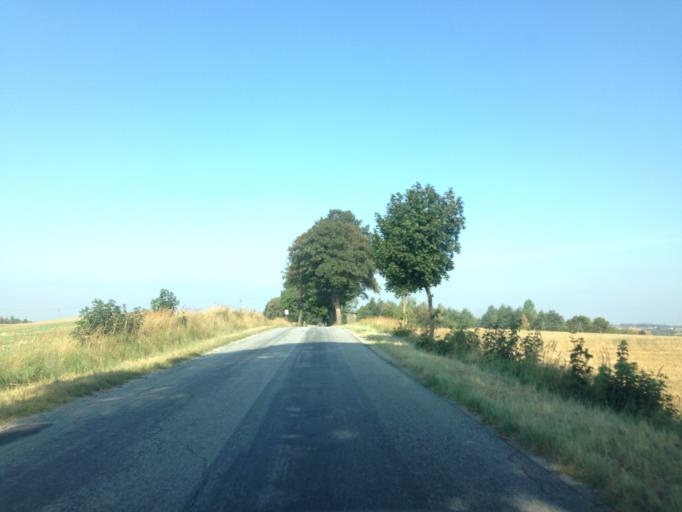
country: PL
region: Kujawsko-Pomorskie
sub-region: Powiat brodnicki
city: Brzozie
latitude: 53.2968
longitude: 19.6338
